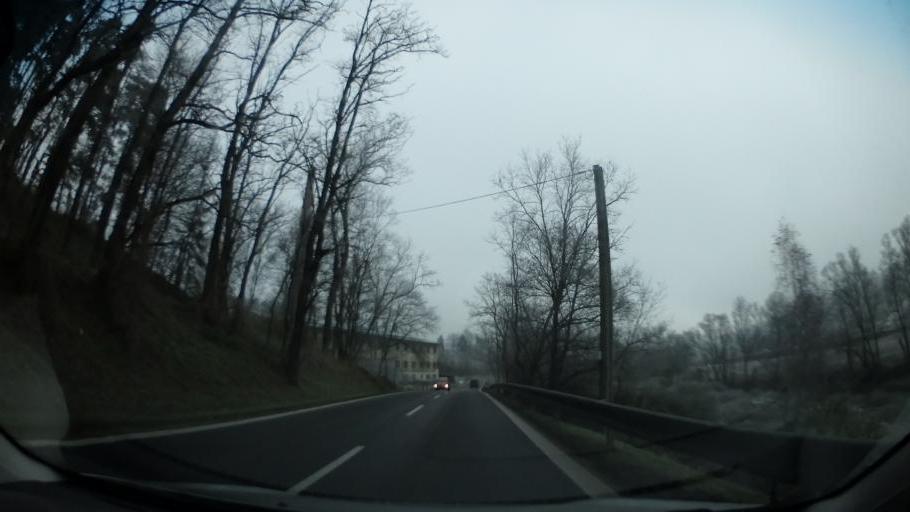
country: CZ
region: Vysocina
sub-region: Okres Trebic
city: Trebic
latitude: 49.2151
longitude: 15.9327
